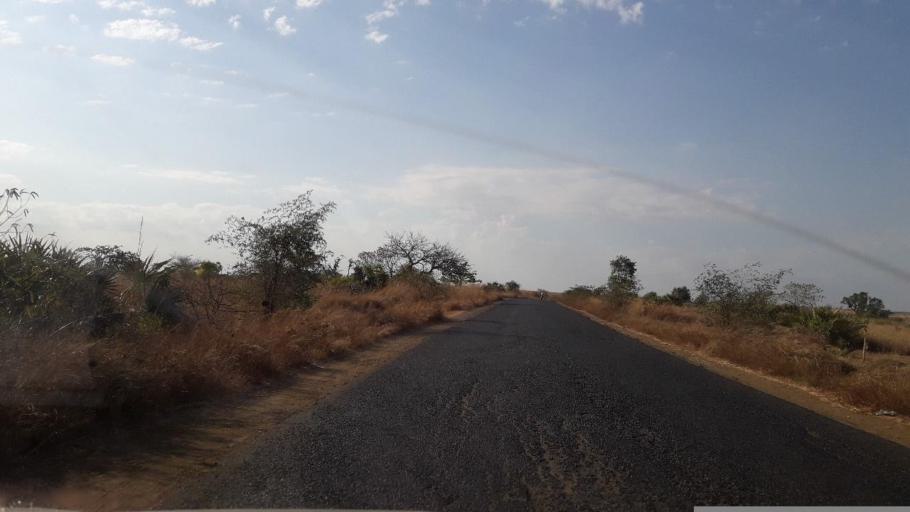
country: MG
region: Boeny
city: Mahajanga
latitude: -15.8608
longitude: 46.5222
